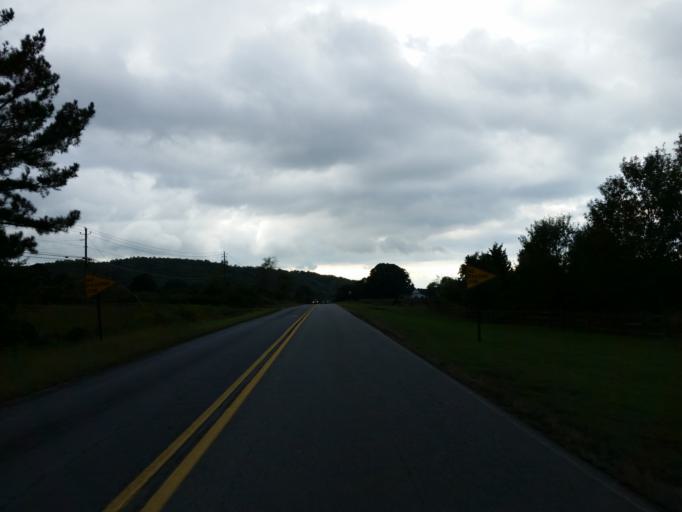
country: US
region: Georgia
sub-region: Bartow County
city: Cartersville
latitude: 34.1172
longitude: -84.8027
